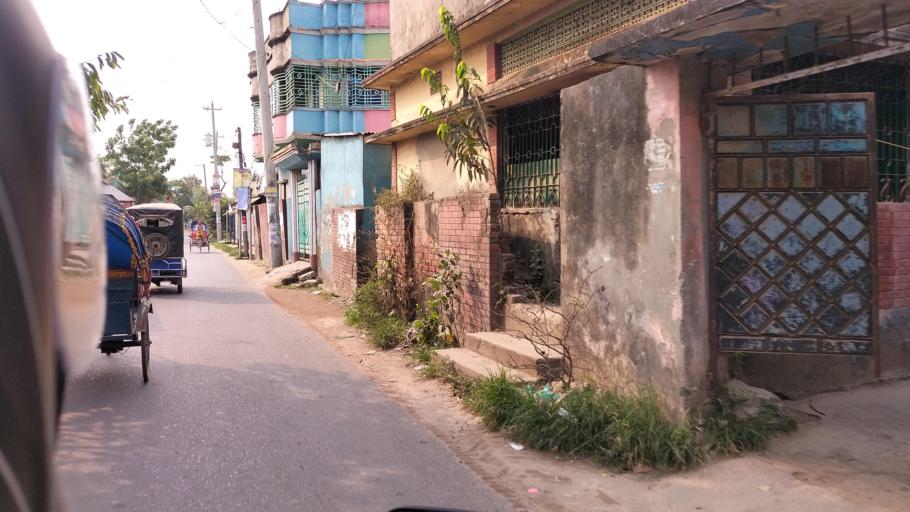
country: BD
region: Dhaka
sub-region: Dhaka
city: Dhaka
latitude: 23.6666
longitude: 90.3496
